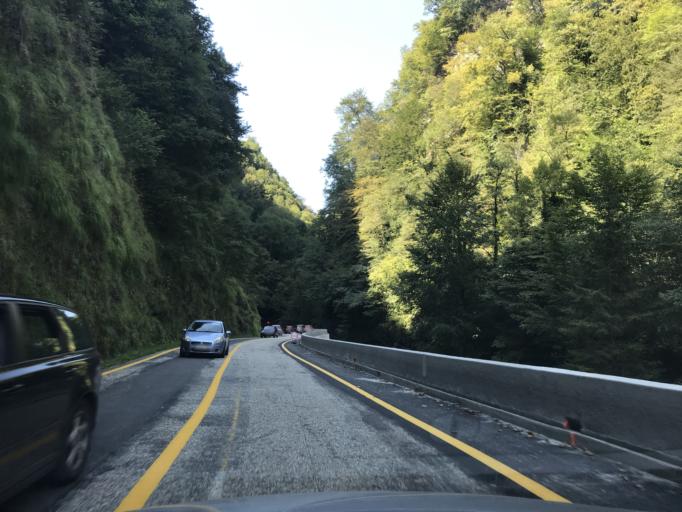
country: FR
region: Rhone-Alpes
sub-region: Departement de la Savoie
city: La Rochette
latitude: 45.4317
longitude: 6.0945
